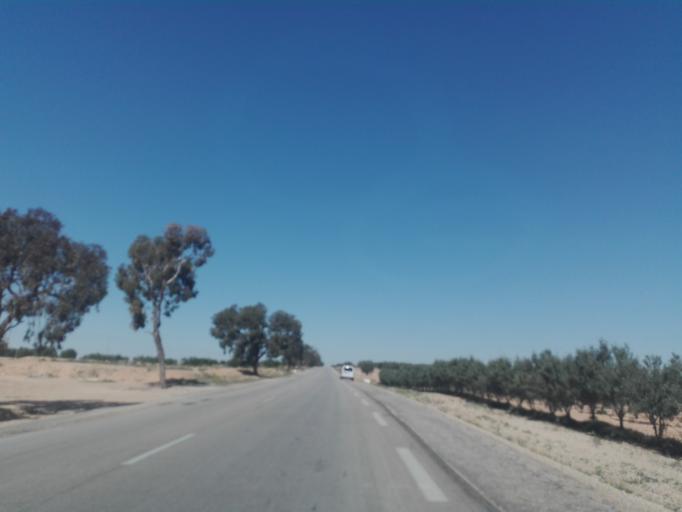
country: TN
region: Safaqis
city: Bi'r `Ali Bin Khalifah
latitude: 34.7505
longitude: 10.3473
